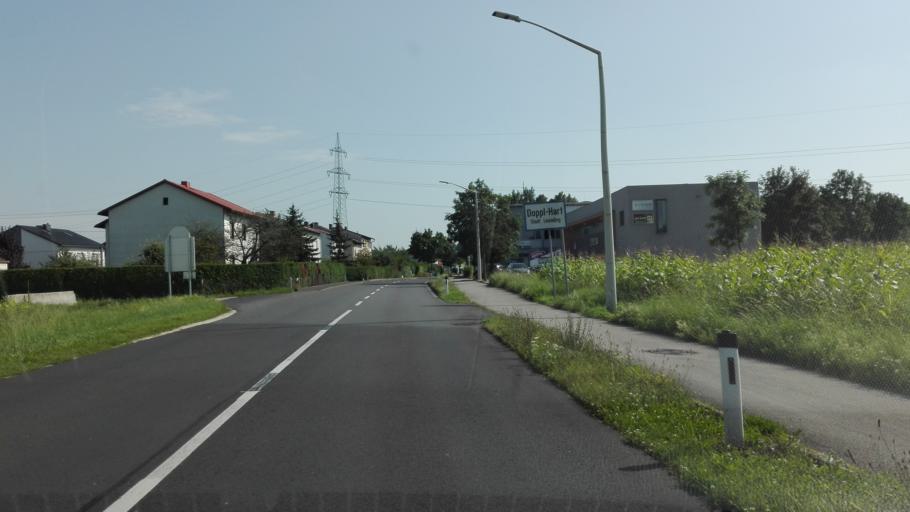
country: AT
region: Upper Austria
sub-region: Politischer Bezirk Linz-Land
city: Leonding
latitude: 48.2539
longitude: 14.2605
